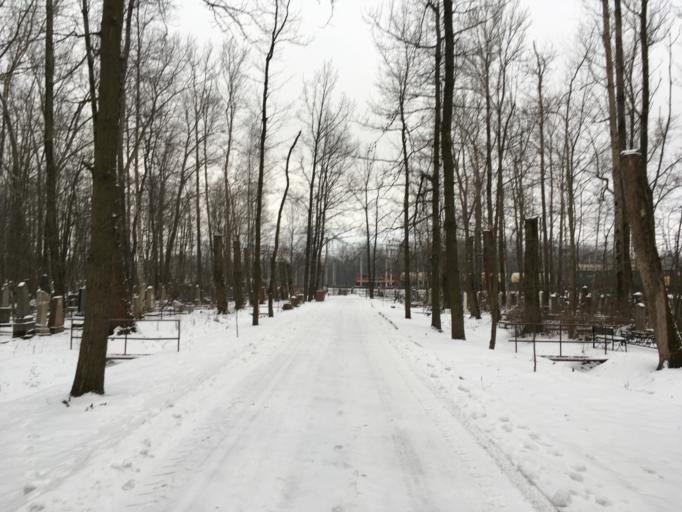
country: RU
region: St.-Petersburg
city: Obukhovo
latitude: 59.8552
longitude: 30.4489
